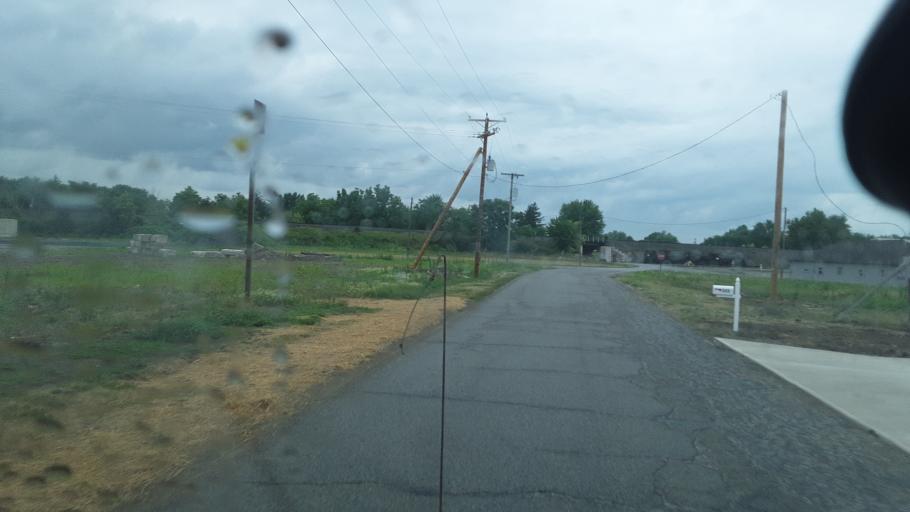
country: US
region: Ohio
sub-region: Defiance County
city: Hicksville
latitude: 41.2945
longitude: -84.7562
